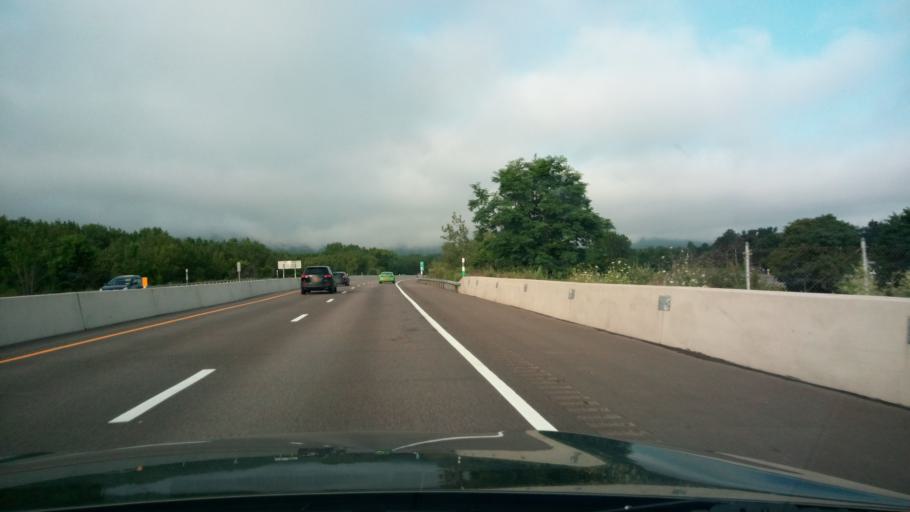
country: US
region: New York
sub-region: Steuben County
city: South Corning
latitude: 42.1234
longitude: -76.9899
